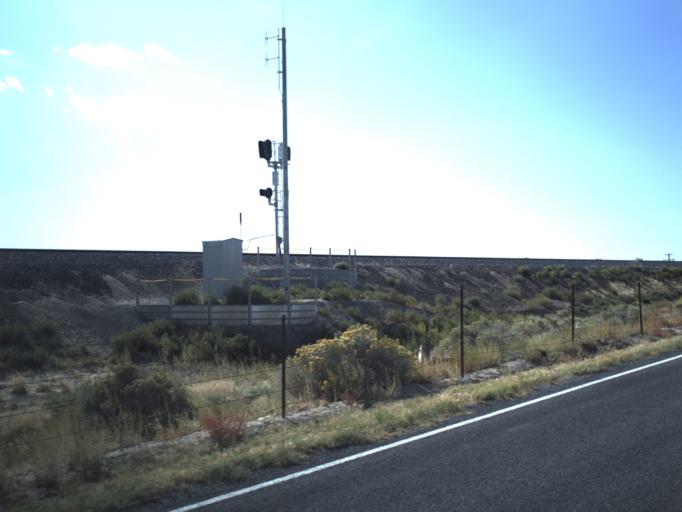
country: US
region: Utah
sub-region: Millard County
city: Delta
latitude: 38.9644
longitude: -112.8017
